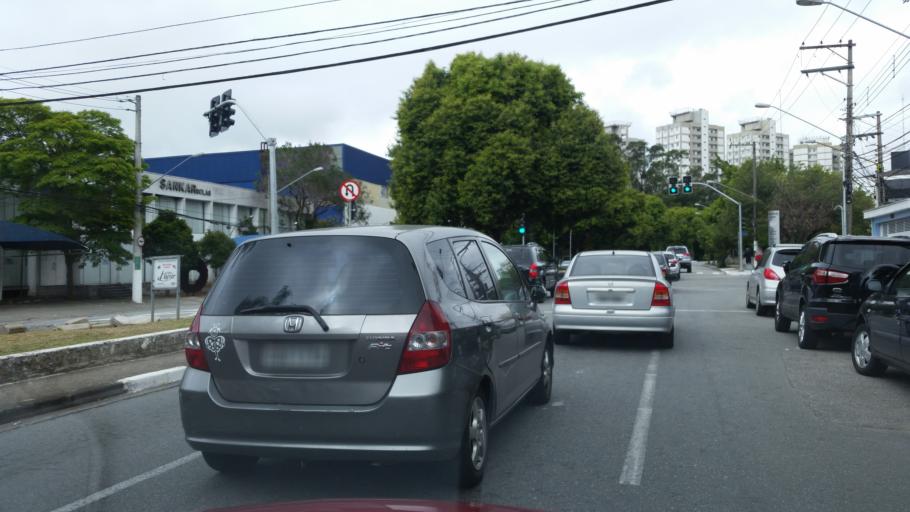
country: BR
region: Sao Paulo
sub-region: Diadema
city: Diadema
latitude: -23.6618
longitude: -46.6883
